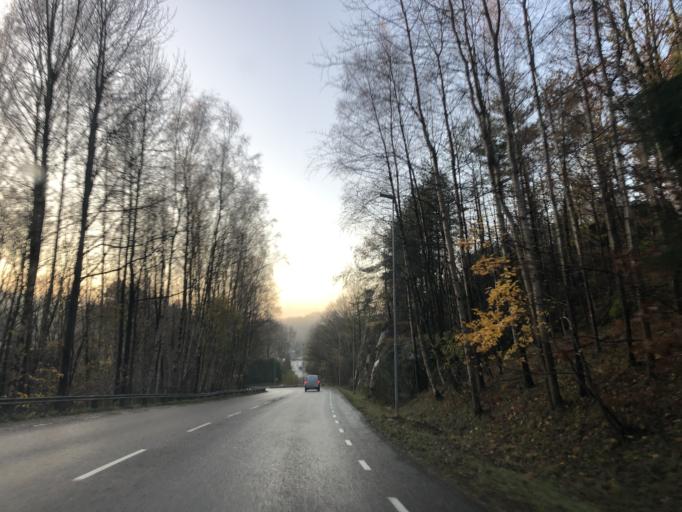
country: SE
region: Vaestra Goetaland
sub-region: Goteborg
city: Gardsten
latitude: 57.7929
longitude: 12.0313
